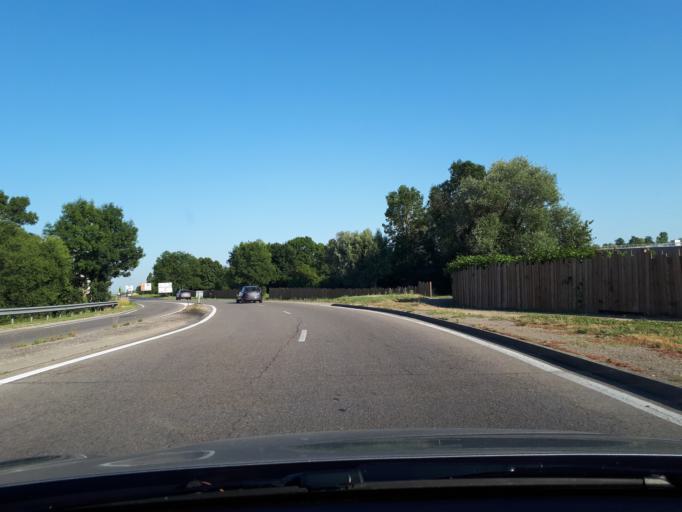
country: FR
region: Rhone-Alpes
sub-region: Departement de l'Isere
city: La Verpilliere
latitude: 45.6290
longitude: 5.1580
